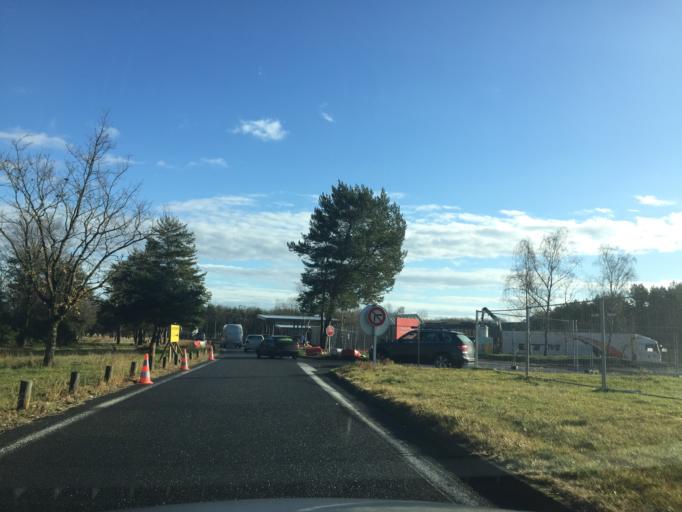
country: FR
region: Auvergne
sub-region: Departement du Puy-de-Dome
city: Orleat
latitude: 45.8513
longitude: 3.4050
